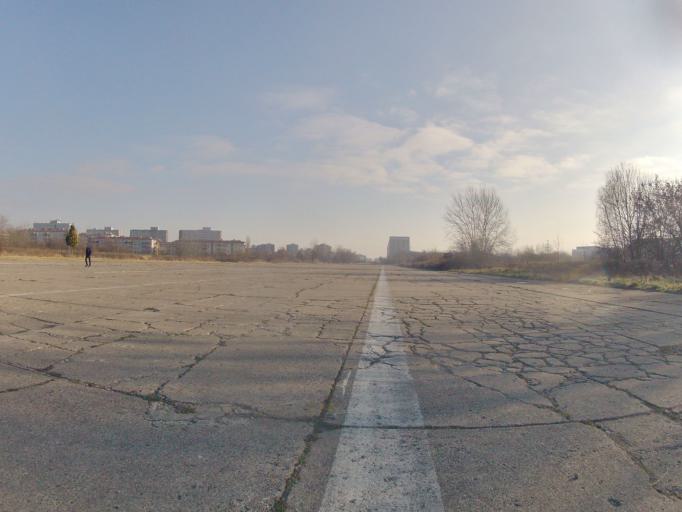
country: PL
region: Lesser Poland Voivodeship
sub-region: Krakow
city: Krakow
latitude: 50.0844
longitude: 19.9894
